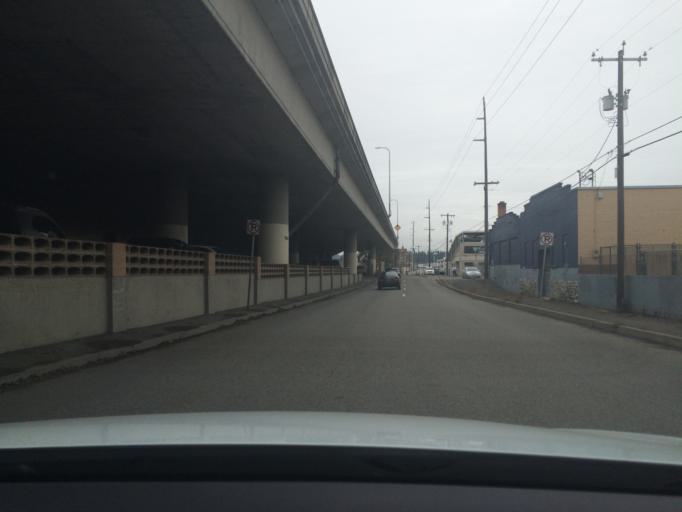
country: US
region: Washington
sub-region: Spokane County
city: Spokane
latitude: 47.6534
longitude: -117.4273
